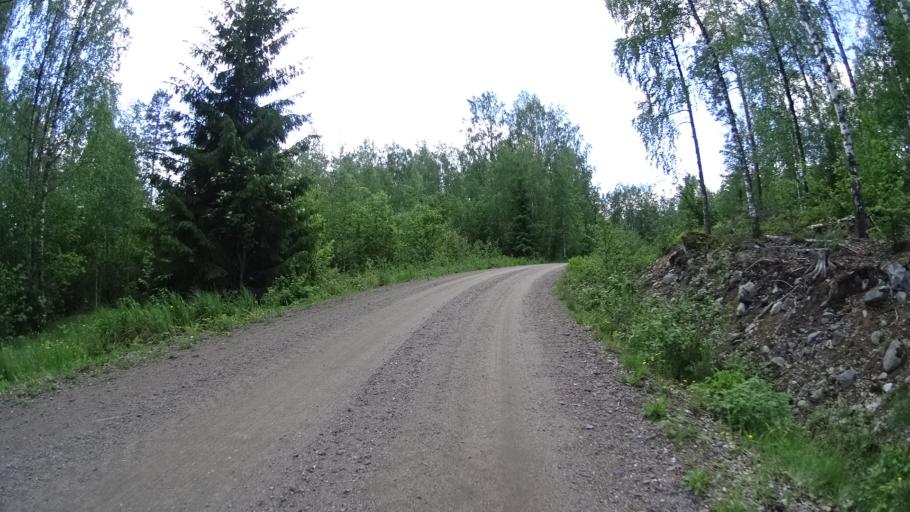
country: FI
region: Uusimaa
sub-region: Raaseporin
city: Karis
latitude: 60.1414
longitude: 23.6199
